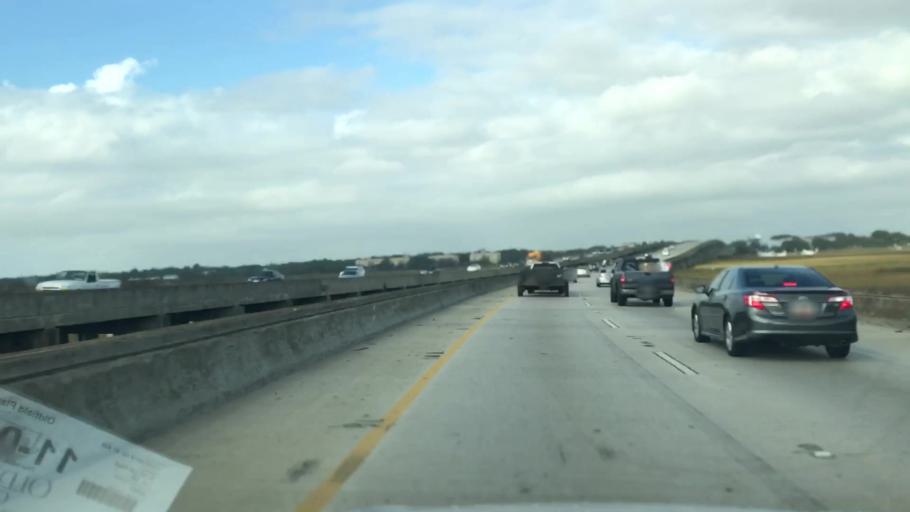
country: US
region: South Carolina
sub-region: Charleston County
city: North Charleston
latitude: 32.8301
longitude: -80.0288
